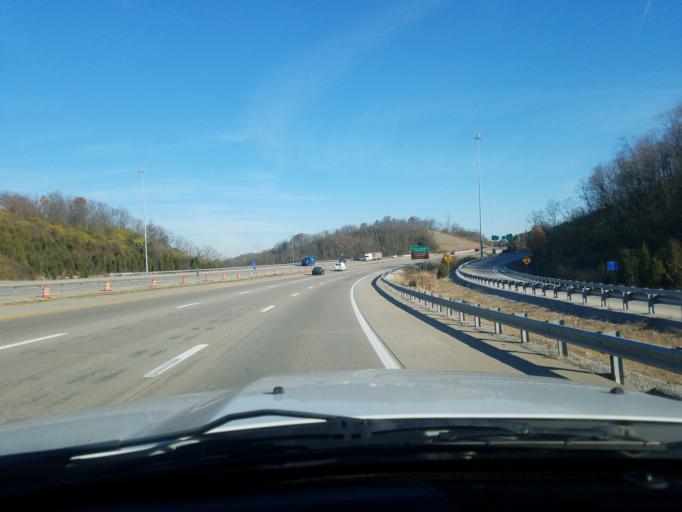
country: US
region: Kentucky
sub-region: Campbell County
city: Highland Heights
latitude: 39.0407
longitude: -84.4697
